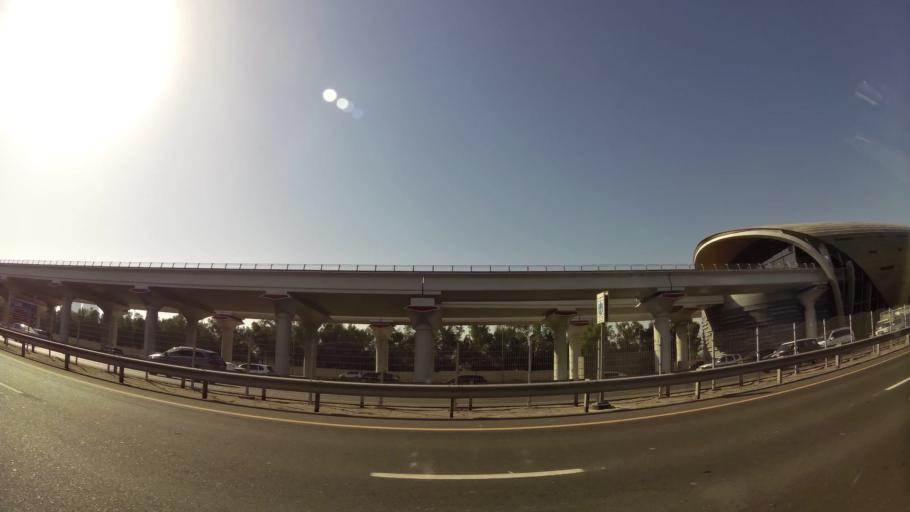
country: AE
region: Dubai
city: Dubai
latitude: 25.0897
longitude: 55.1582
